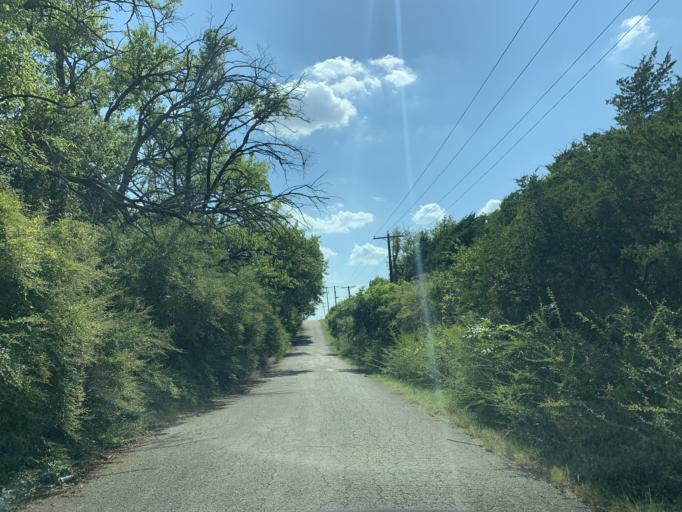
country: US
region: Texas
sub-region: Dallas County
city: Lancaster
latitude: 32.6546
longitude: -96.7851
